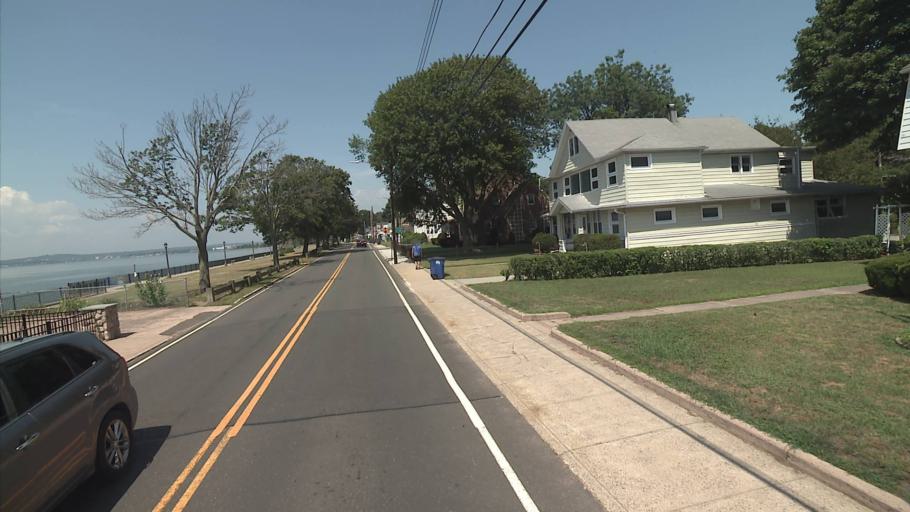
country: US
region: Connecticut
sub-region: New Haven County
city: East Haven
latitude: 41.2616
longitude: -72.8940
